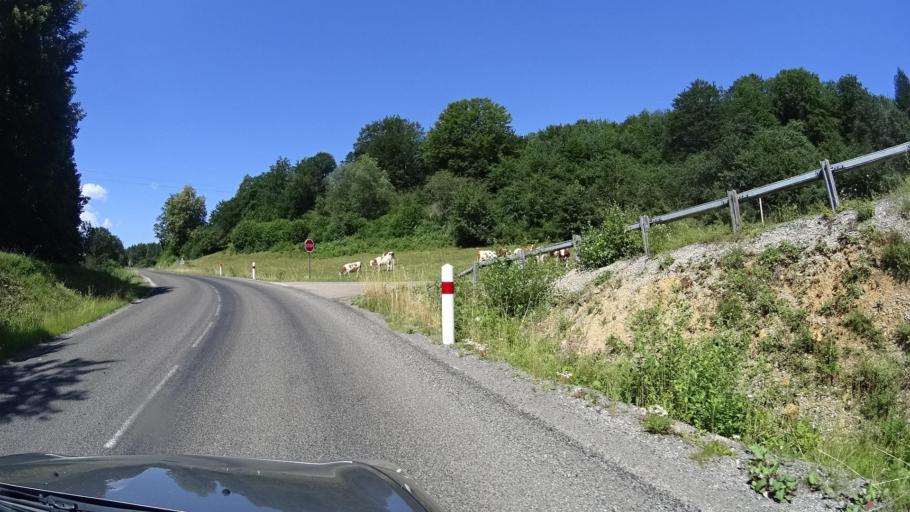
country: FR
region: Franche-Comte
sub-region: Departement du Jura
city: Longchaumois
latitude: 46.5054
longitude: 5.9444
